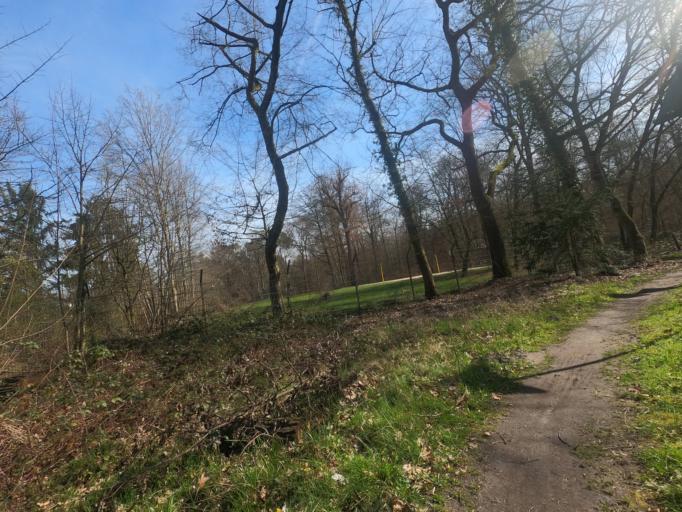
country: DE
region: Hesse
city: Morfelden-Walldorf
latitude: 49.9707
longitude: 8.5500
